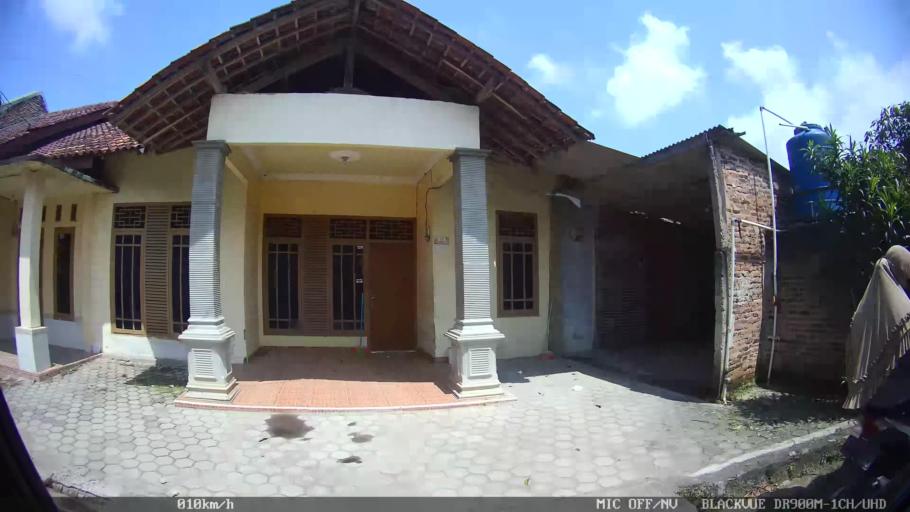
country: ID
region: Lampung
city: Kedaton
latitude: -5.3498
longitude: 105.2836
